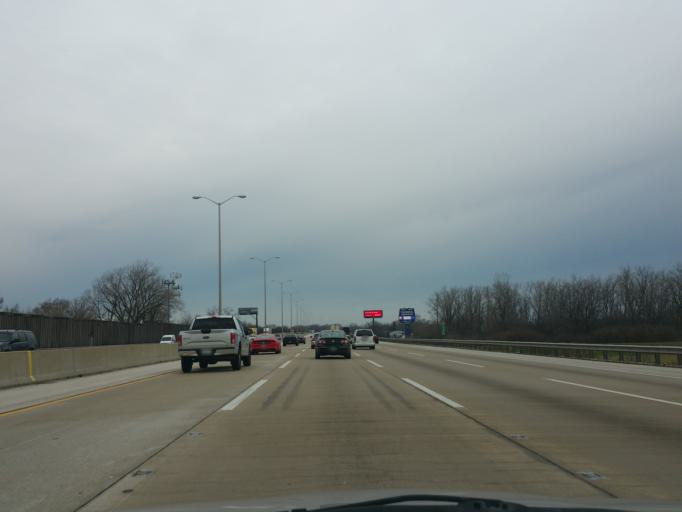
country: US
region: Illinois
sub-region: Cook County
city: Chicago Ridge
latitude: 41.6783
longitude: -87.7741
